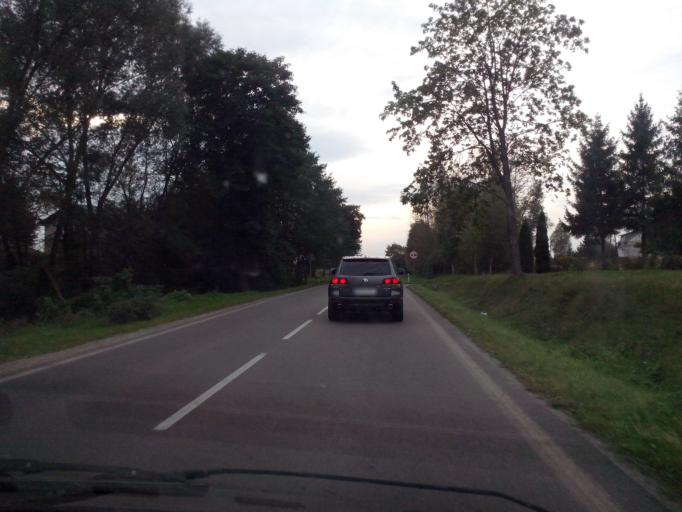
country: PL
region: Subcarpathian Voivodeship
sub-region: Powiat przemyski
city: Przedmiescie Dubieckie
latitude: 49.8249
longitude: 22.3431
